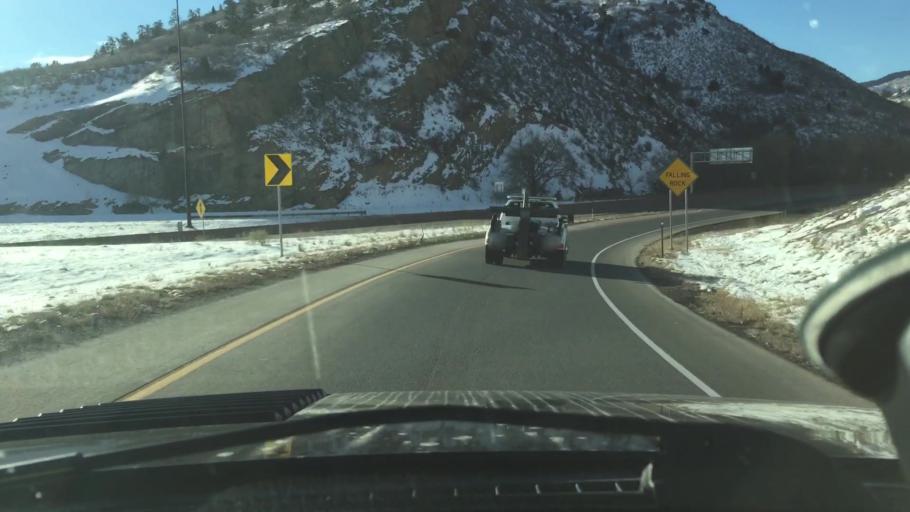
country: US
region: Colorado
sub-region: Jefferson County
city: Indian Hills
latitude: 39.6362
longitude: -105.1692
